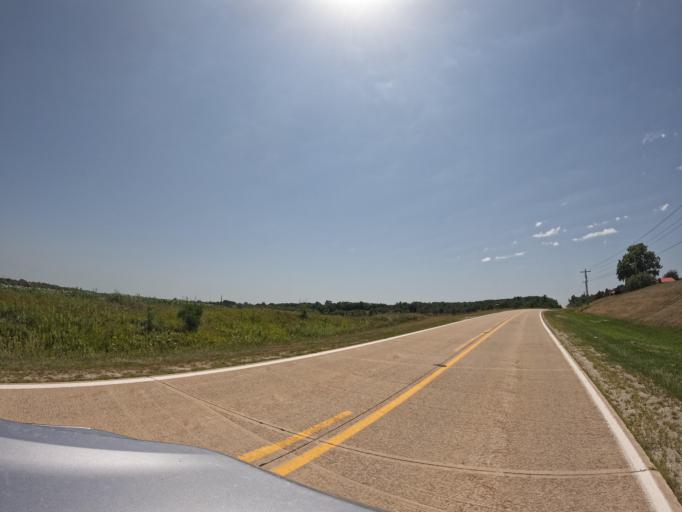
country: US
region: Iowa
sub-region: Henry County
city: Mount Pleasant
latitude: 40.9213
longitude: -91.5539
